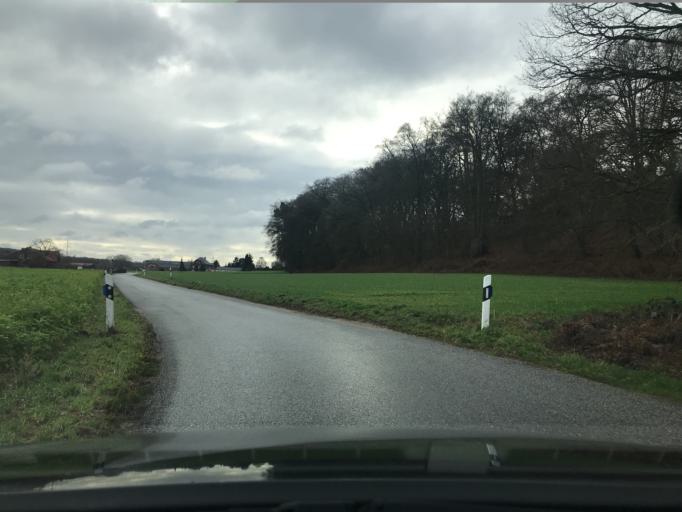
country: DE
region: North Rhine-Westphalia
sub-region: Regierungsbezirk Dusseldorf
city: Rheurdt
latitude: 51.4068
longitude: 6.5255
